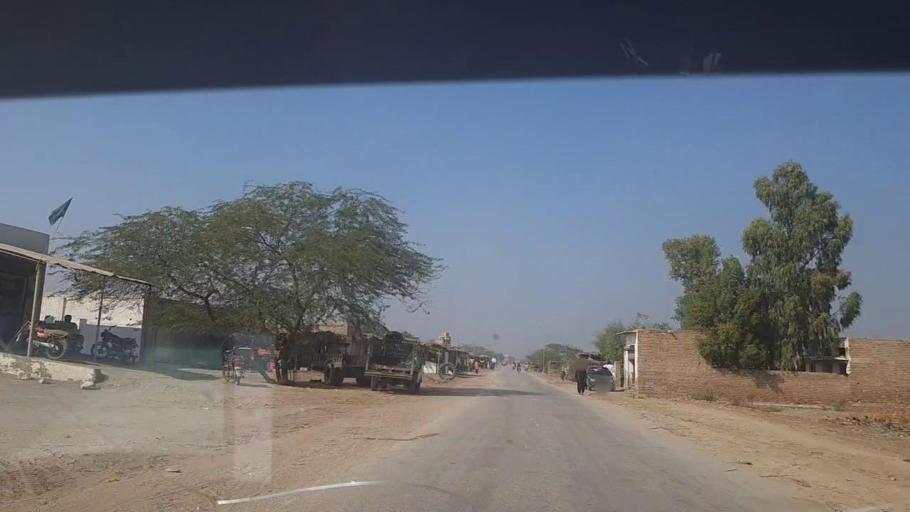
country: PK
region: Sindh
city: Kot Diji
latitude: 27.4130
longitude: 68.6664
